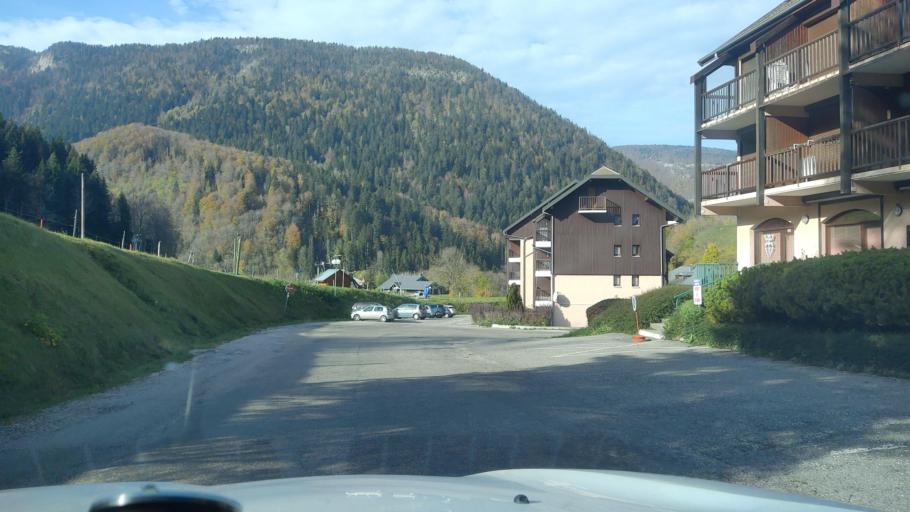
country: FR
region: Rhone-Alpes
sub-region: Departement de la Savoie
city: Cruet
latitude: 45.6086
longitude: 6.1058
